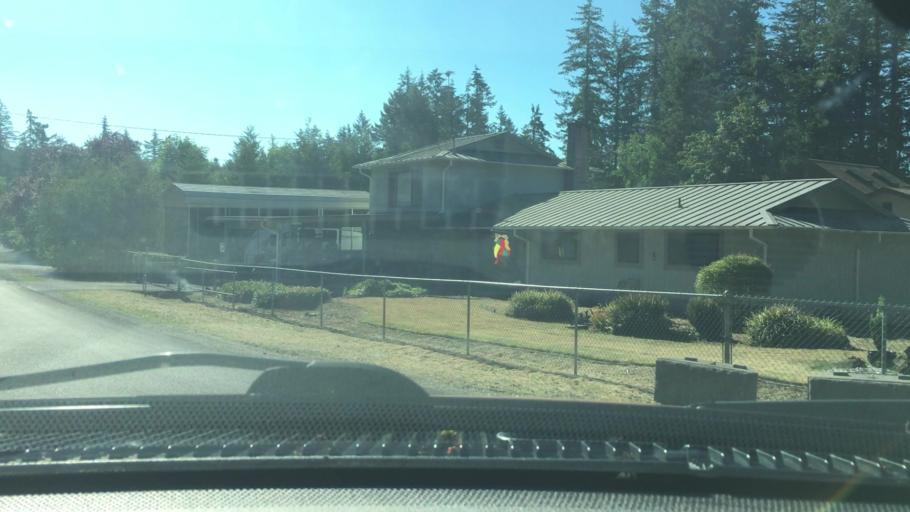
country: US
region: Washington
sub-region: King County
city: Lake Morton-Berrydale
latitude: 47.3211
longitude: -122.1026
